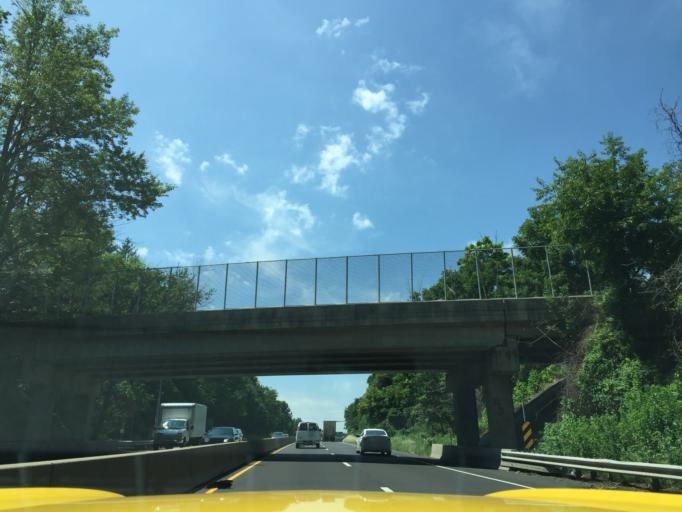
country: US
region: Pennsylvania
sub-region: Bucks County
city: Langhorne Manor
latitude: 40.1738
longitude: -74.9111
